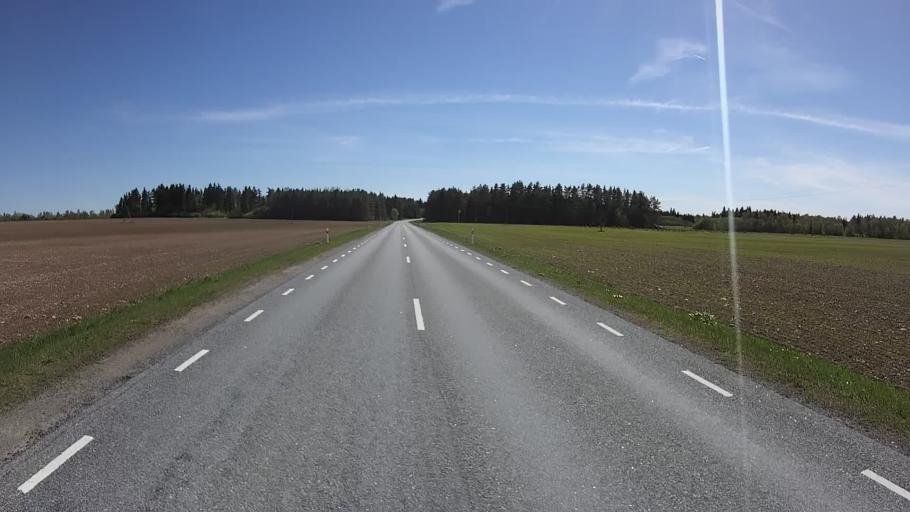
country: EE
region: Laeaene-Virumaa
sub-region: Tapa vald
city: Tapa
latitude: 59.2902
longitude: 25.9976
